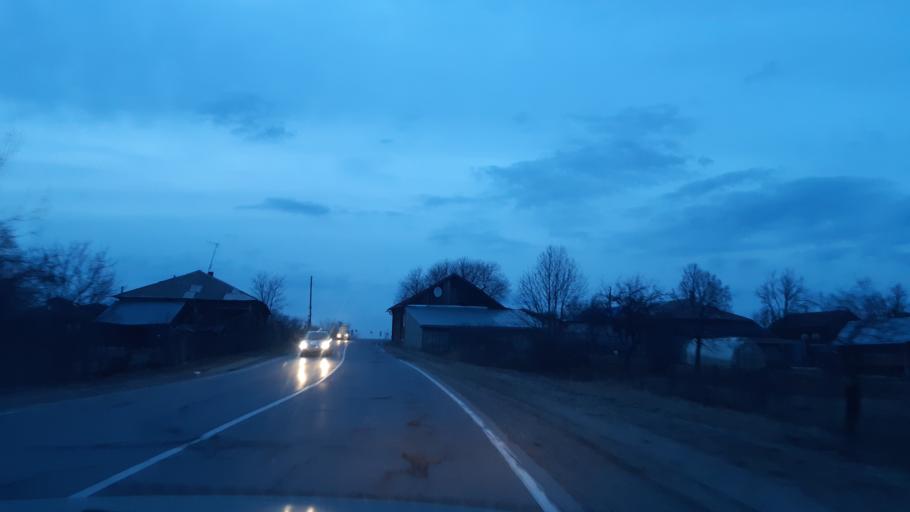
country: RU
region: Vladimir
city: Luknovo
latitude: 56.2134
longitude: 42.0309
